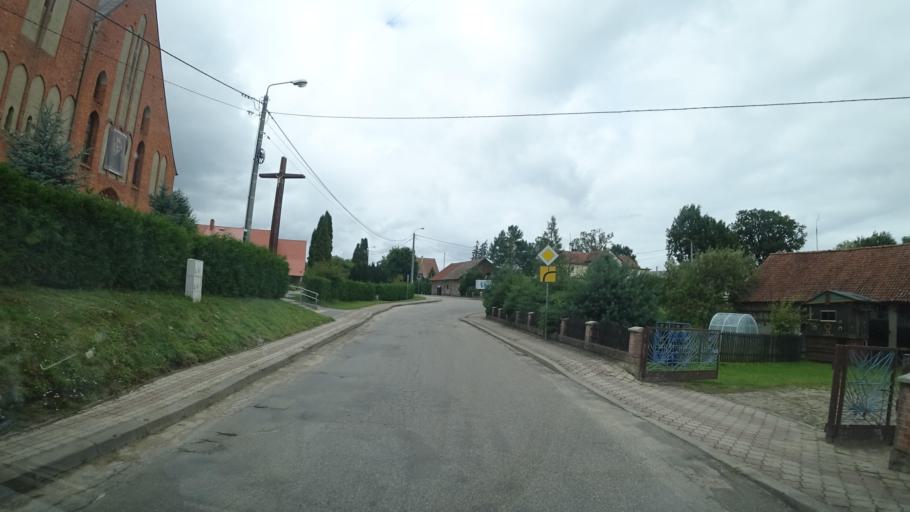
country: PL
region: Podlasie
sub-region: Powiat suwalski
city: Filipow
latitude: 54.2875
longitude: 22.5569
